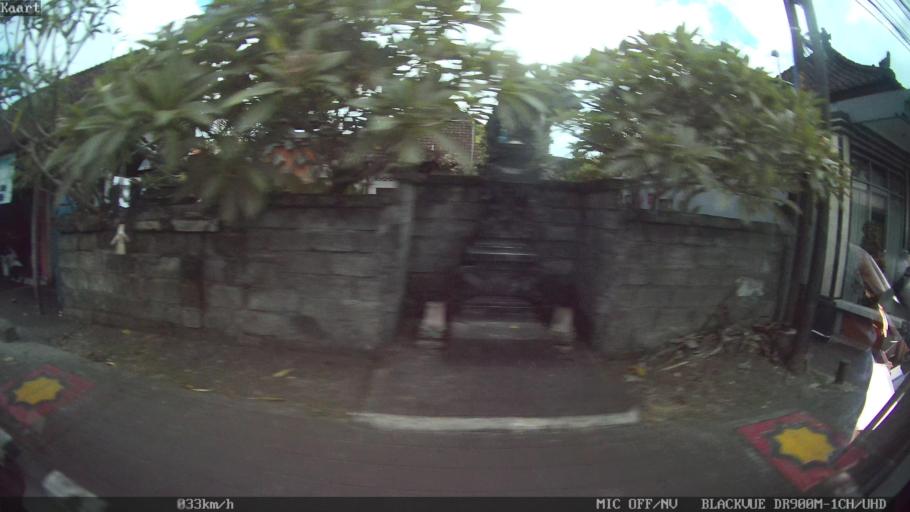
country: ID
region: Bali
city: Banjar Pekenjelodan
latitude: -8.5923
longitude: 115.1758
